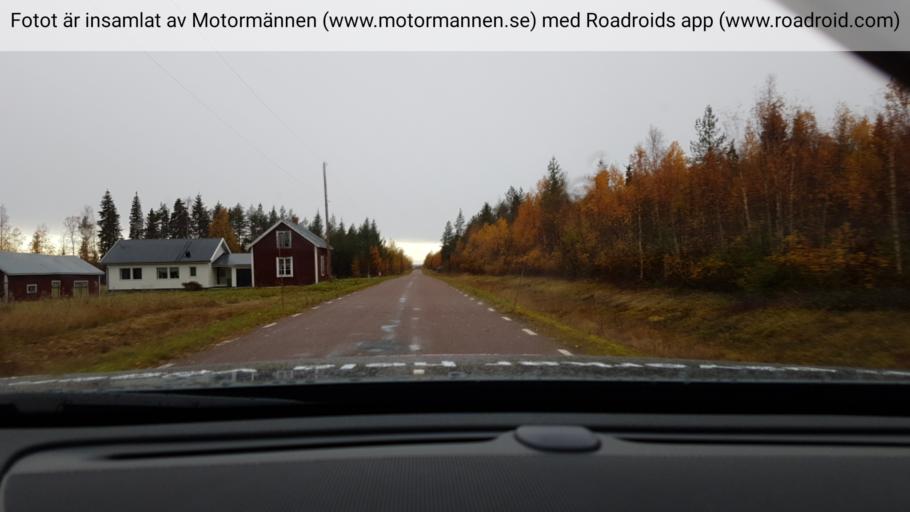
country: SE
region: Norrbotten
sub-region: Pajala Kommun
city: Pajala
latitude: 66.9576
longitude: 22.9584
